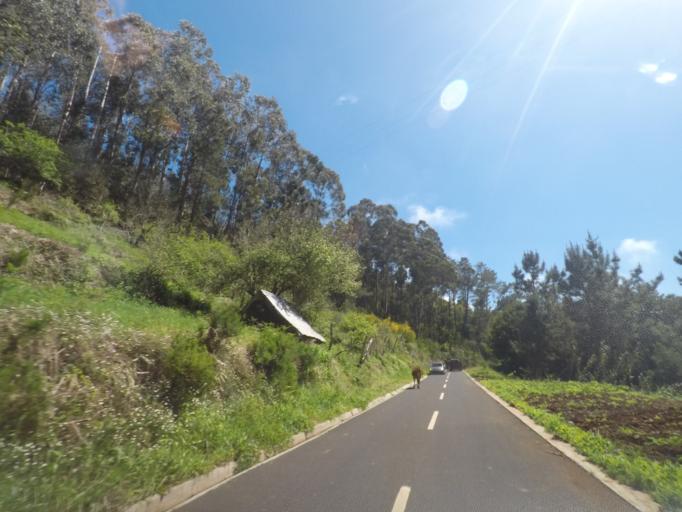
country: PT
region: Madeira
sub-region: Calheta
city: Arco da Calheta
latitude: 32.7249
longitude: -17.1179
